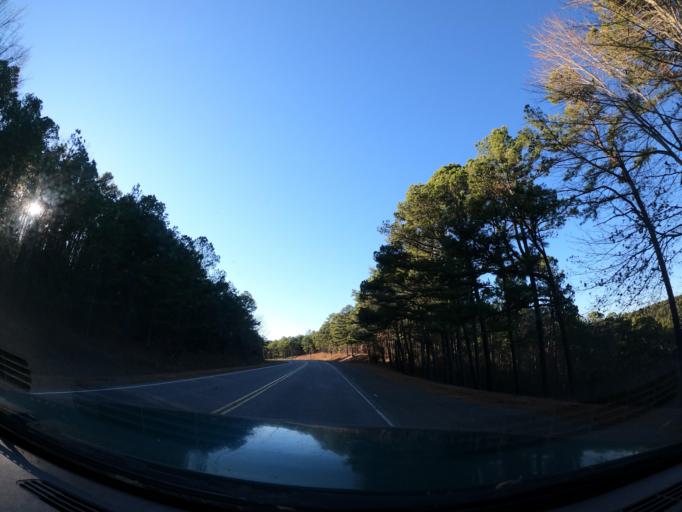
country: US
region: Oklahoma
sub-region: Latimer County
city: Wilburton
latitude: 35.0009
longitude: -95.3384
